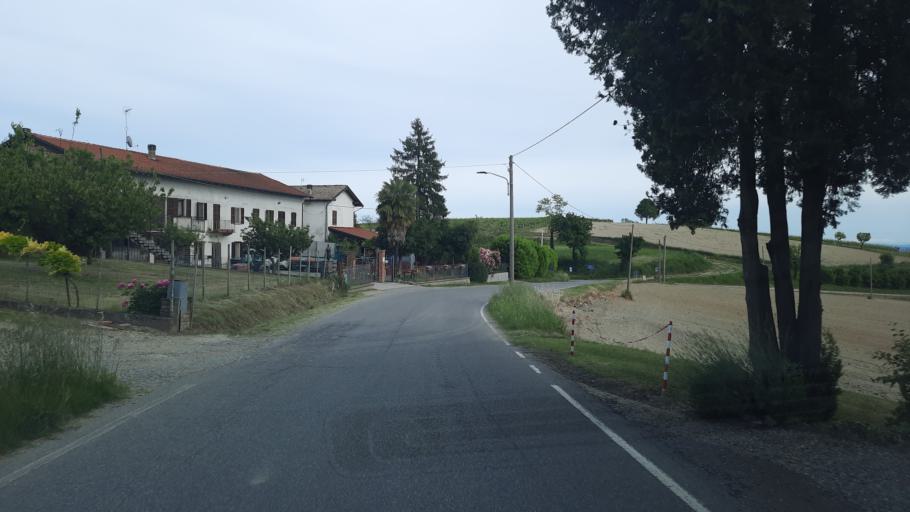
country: IT
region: Piedmont
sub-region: Provincia di Alessandria
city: Alfiano Natta
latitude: 45.0456
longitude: 8.2188
